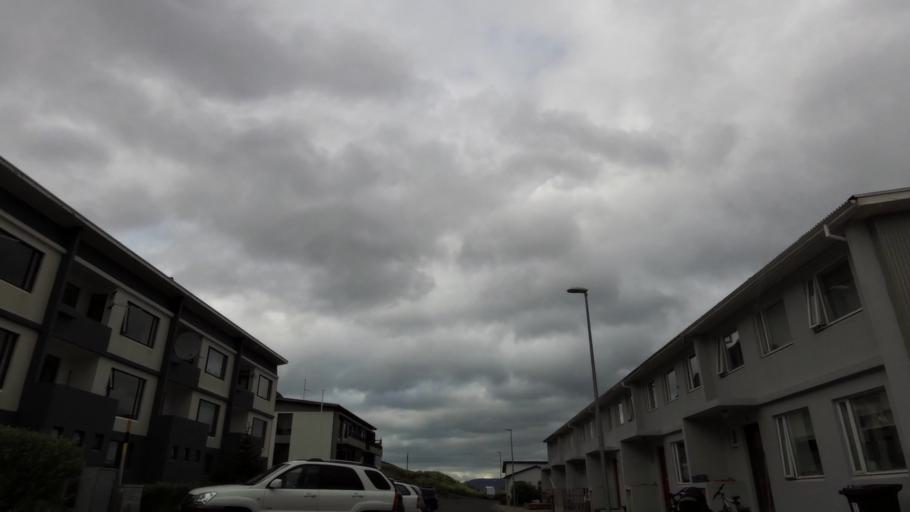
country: IS
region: Westfjords
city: Isafjoerdur
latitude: 66.0790
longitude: -23.1262
